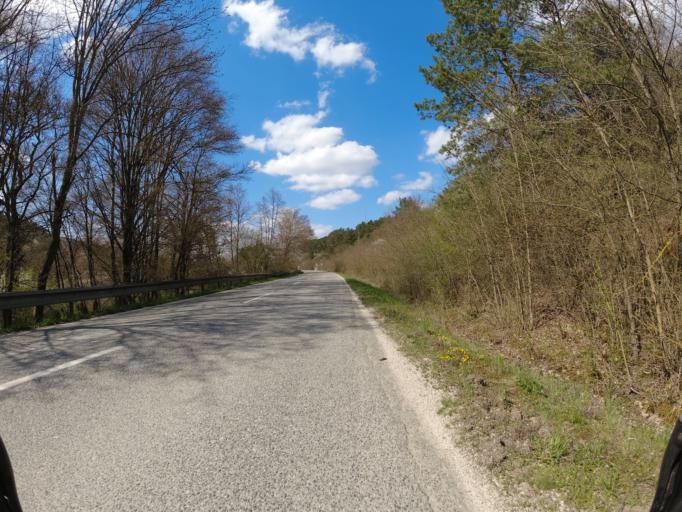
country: SK
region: Nitriansky
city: Stara Tura
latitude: 48.7506
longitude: 17.7222
